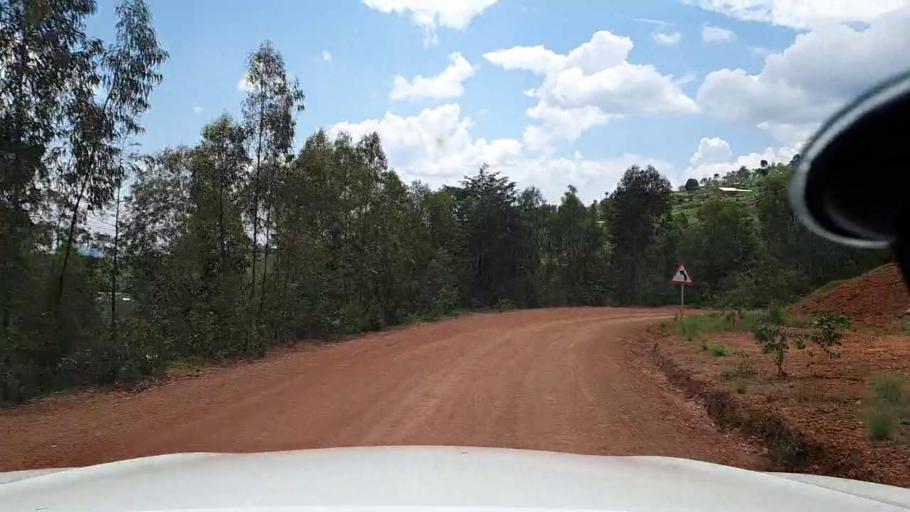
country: RW
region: Kigali
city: Kigali
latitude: -1.7875
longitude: 29.8454
